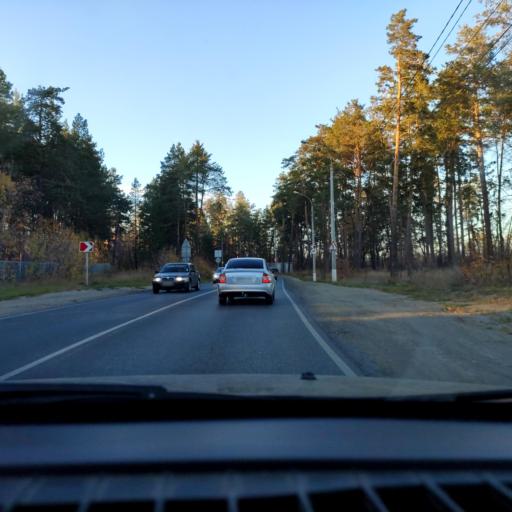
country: RU
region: Samara
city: Tol'yatti
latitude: 53.4869
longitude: 49.3113
